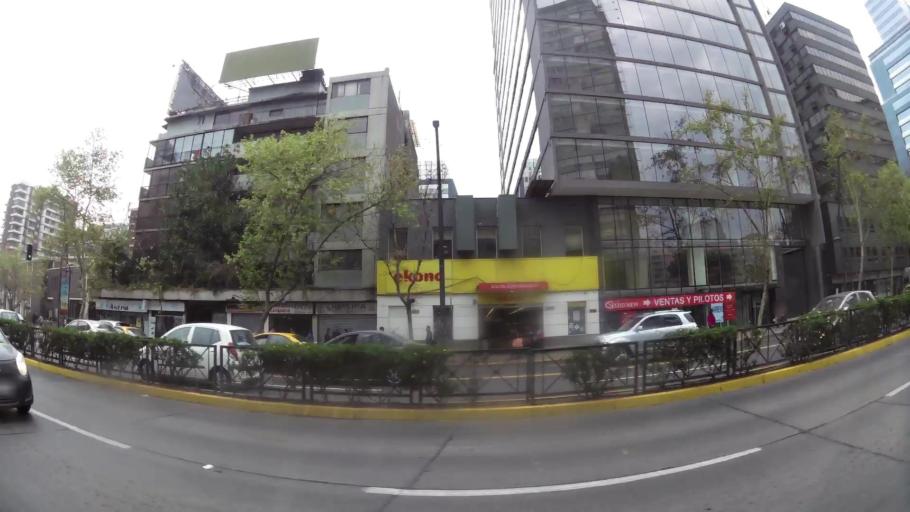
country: CL
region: Santiago Metropolitan
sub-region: Provincia de Santiago
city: Santiago
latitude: -33.4269
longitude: -70.6161
